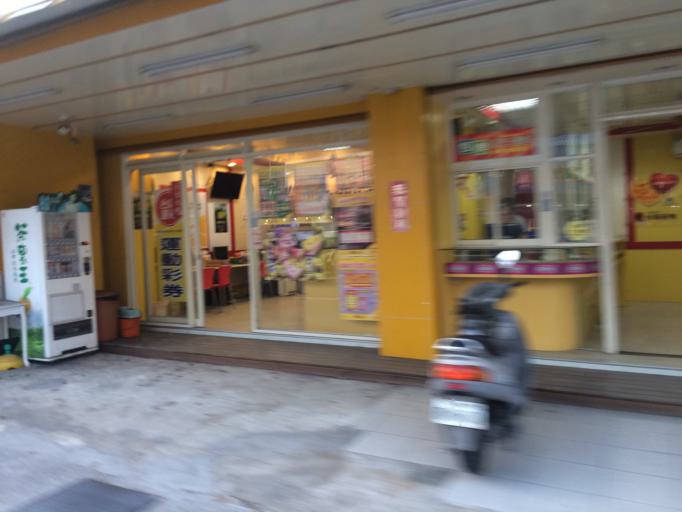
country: TW
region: Taiwan
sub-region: Hsinchu
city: Hsinchu
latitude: 24.6908
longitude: 120.9131
